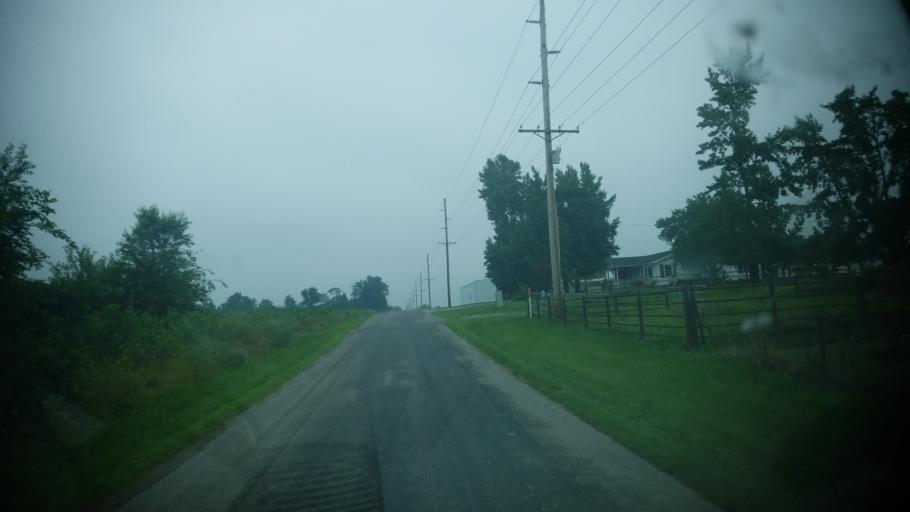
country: US
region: Illinois
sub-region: Wayne County
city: Fairfield
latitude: 38.5223
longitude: -88.4024
